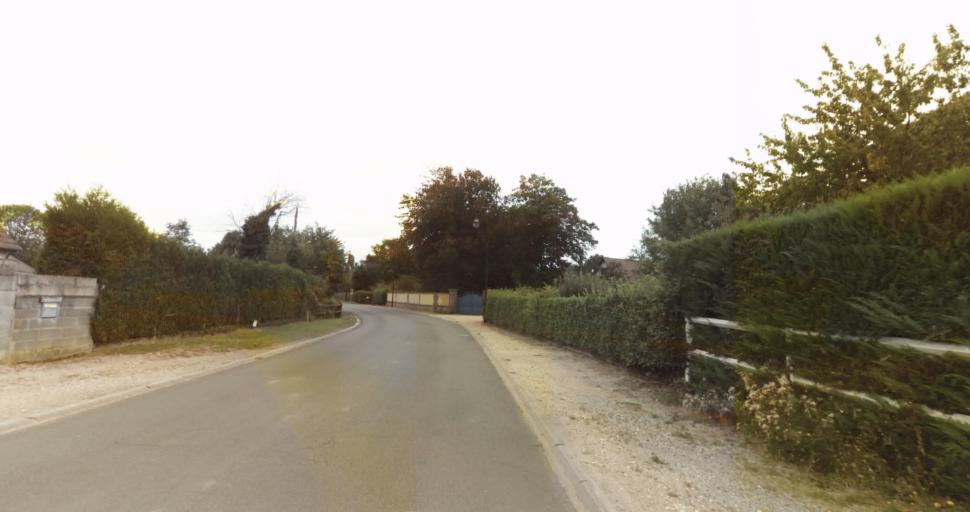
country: FR
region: Haute-Normandie
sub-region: Departement de l'Eure
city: Gravigny
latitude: 48.9915
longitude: 1.2450
